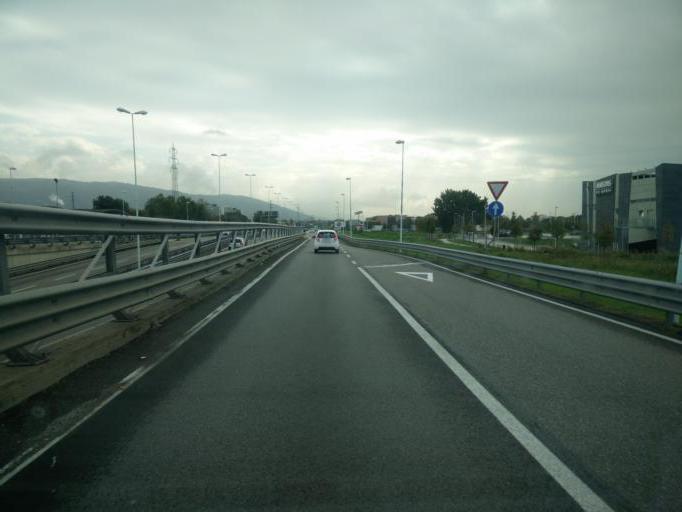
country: IT
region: Tuscany
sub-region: Provincia di Prato
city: Prato
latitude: 43.8786
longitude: 11.0643
